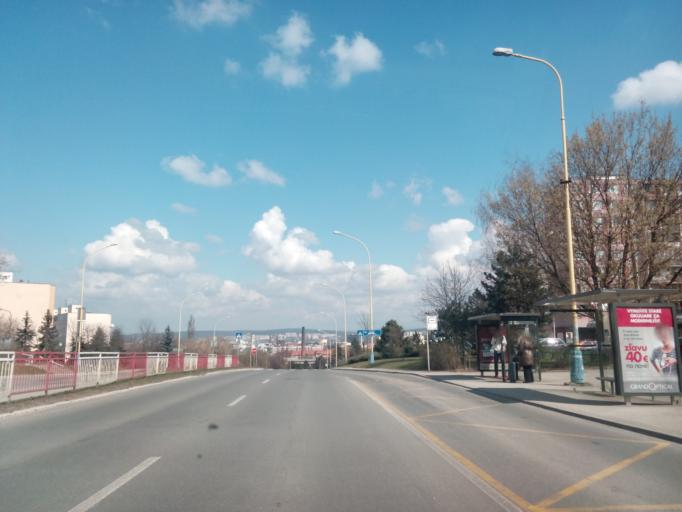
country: SK
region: Kosicky
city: Kosice
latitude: 48.7022
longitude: 21.2532
